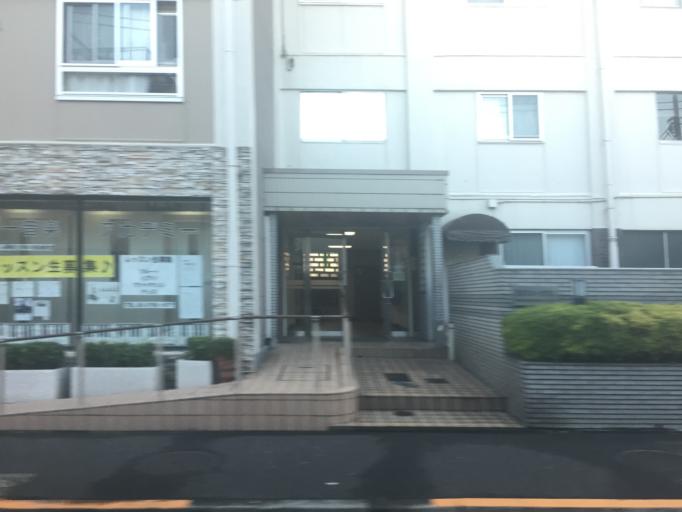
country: JP
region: Tokyo
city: Tokyo
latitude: 35.6204
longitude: 139.6412
